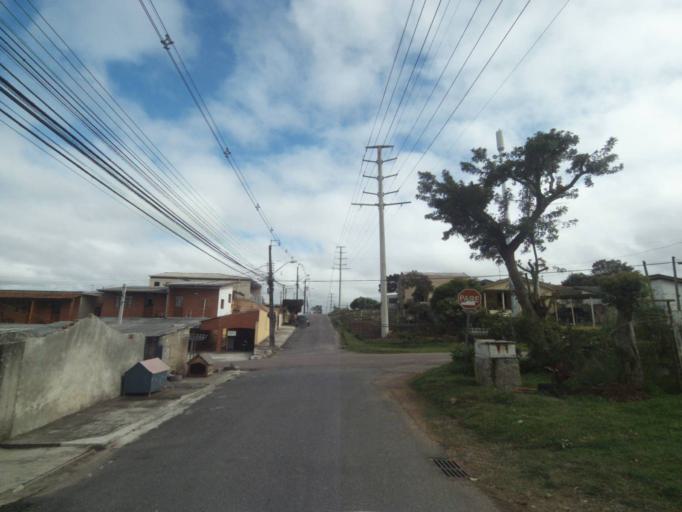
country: BR
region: Parana
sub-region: Sao Jose Dos Pinhais
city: Sao Jose dos Pinhais
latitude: -25.5226
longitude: -49.3018
